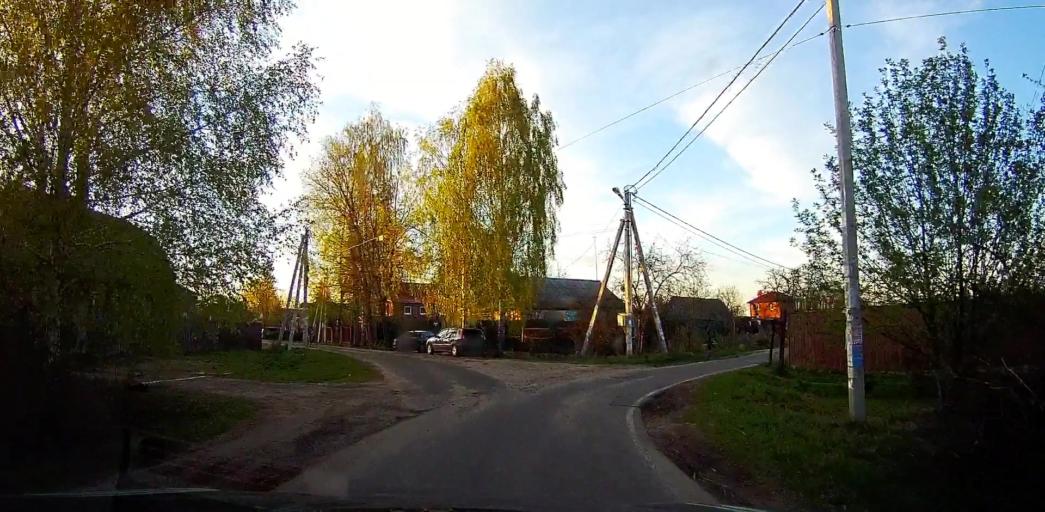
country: RU
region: Moskovskaya
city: Peski
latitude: 55.2095
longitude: 38.7392
